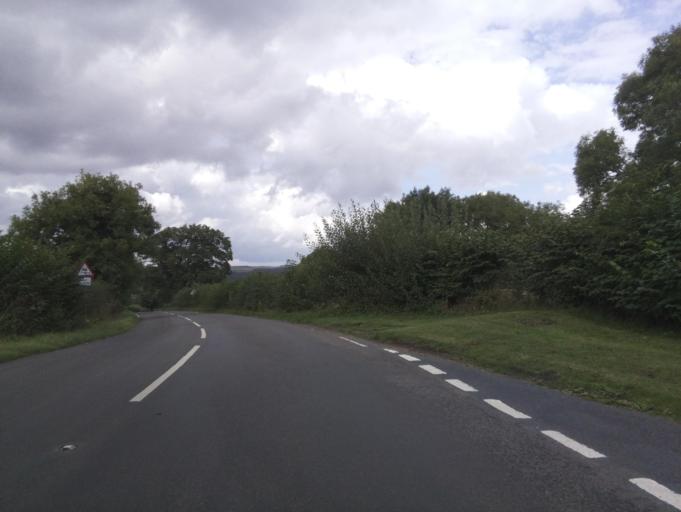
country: GB
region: England
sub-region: North Yorkshire
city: Leyburn
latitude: 54.3765
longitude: -1.8297
